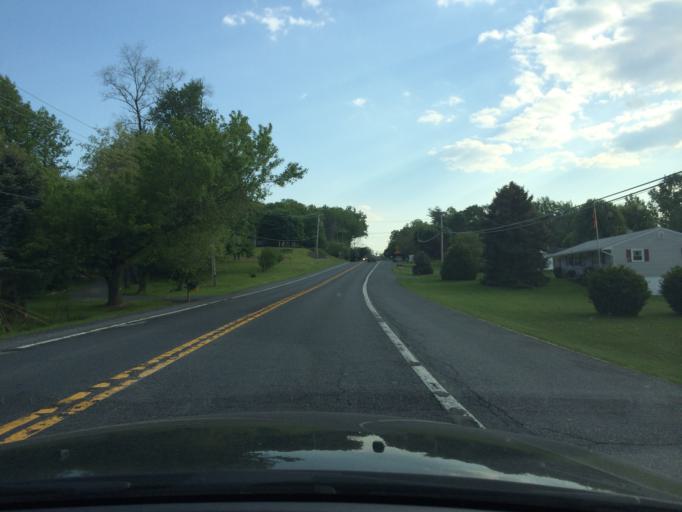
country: US
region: Maryland
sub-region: Carroll County
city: Westminster
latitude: 39.5277
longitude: -77.0259
